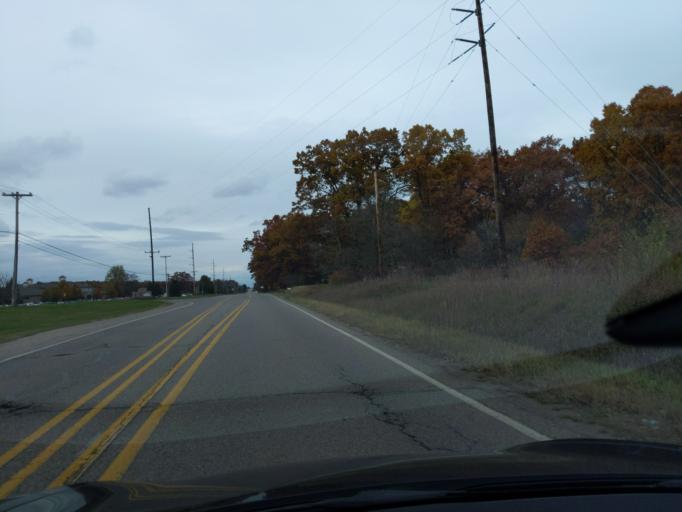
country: US
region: Michigan
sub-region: Clinton County
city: Bath
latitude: 42.7877
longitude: -84.4836
